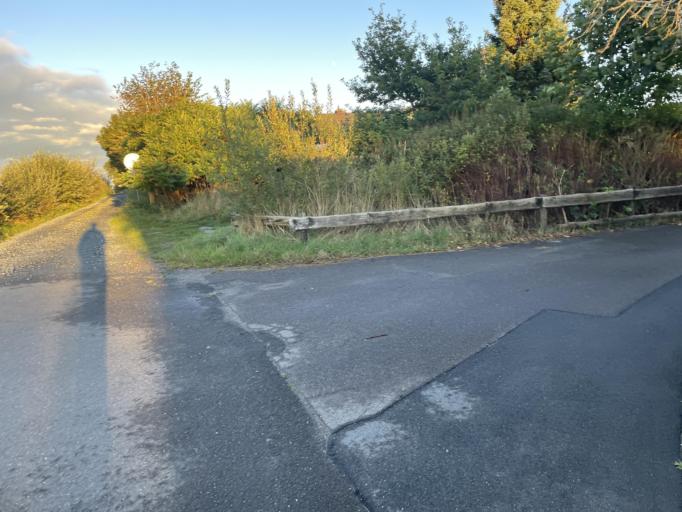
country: DE
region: Schleswig-Holstein
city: Mildstedt
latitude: 54.4776
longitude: 9.1057
